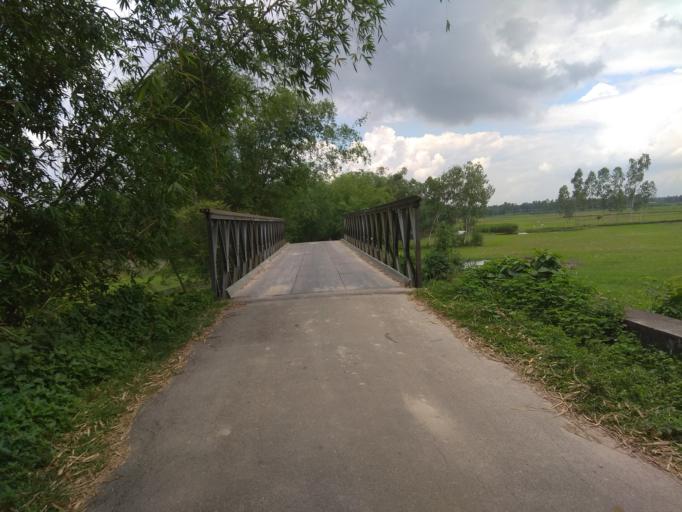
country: IN
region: West Bengal
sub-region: Koch Bihar
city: Haldibari
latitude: 26.2050
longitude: 88.9181
